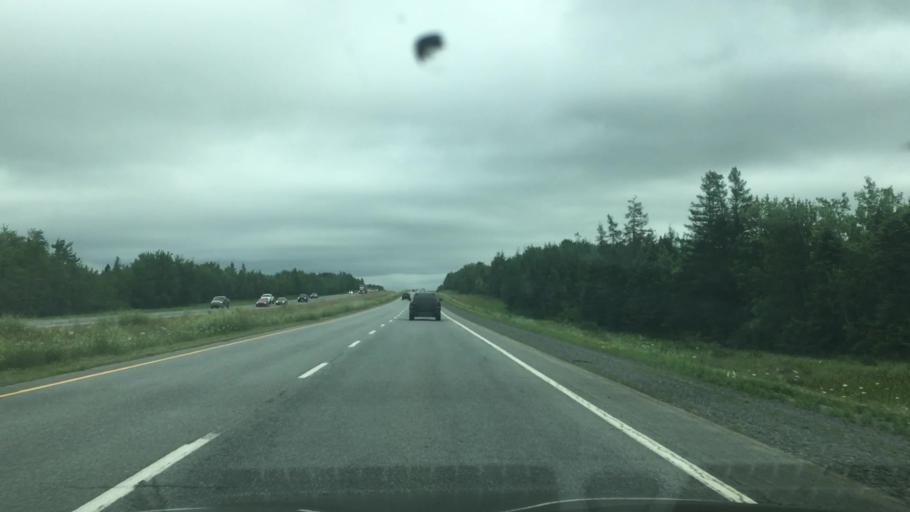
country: CA
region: Nova Scotia
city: Cole Harbour
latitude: 44.9983
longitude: -63.4894
